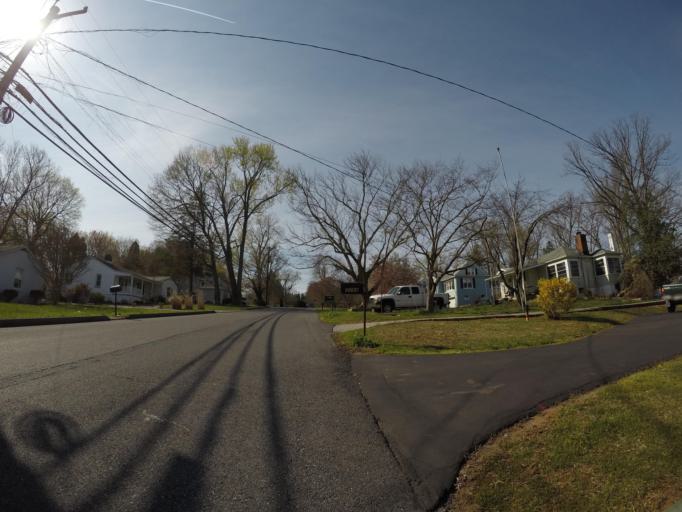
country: US
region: Maryland
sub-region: Howard County
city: Ellicott City
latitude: 39.2750
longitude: -76.8319
